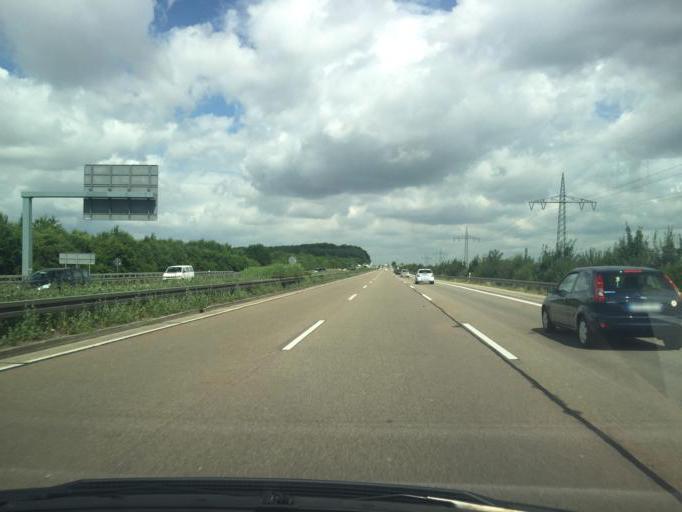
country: DE
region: Hesse
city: Bad Camberg
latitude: 50.3120
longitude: 8.2296
